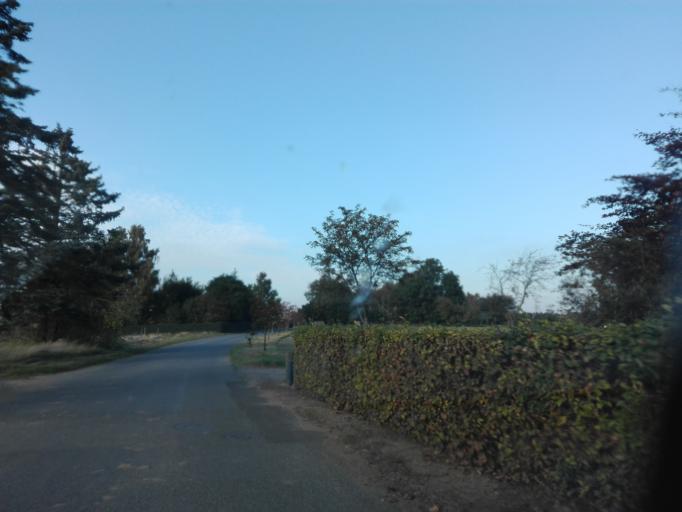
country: DK
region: Central Jutland
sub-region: Odder Kommune
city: Odder
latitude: 55.9453
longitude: 10.1948
